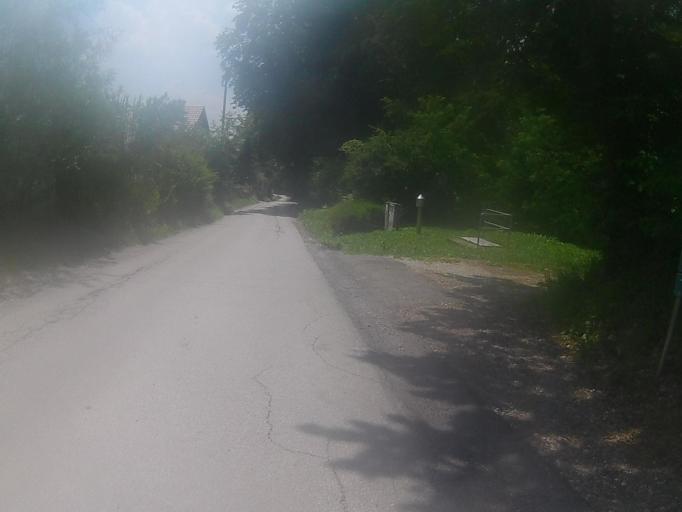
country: SI
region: Maribor
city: Kamnica
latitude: 46.5923
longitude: 15.6163
